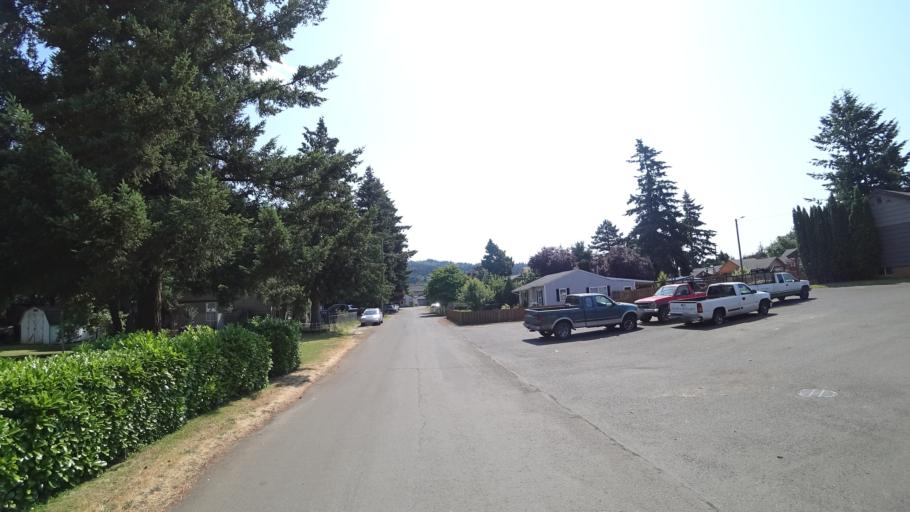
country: US
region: Oregon
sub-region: Multnomah County
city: Lents
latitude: 45.4525
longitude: -122.5824
